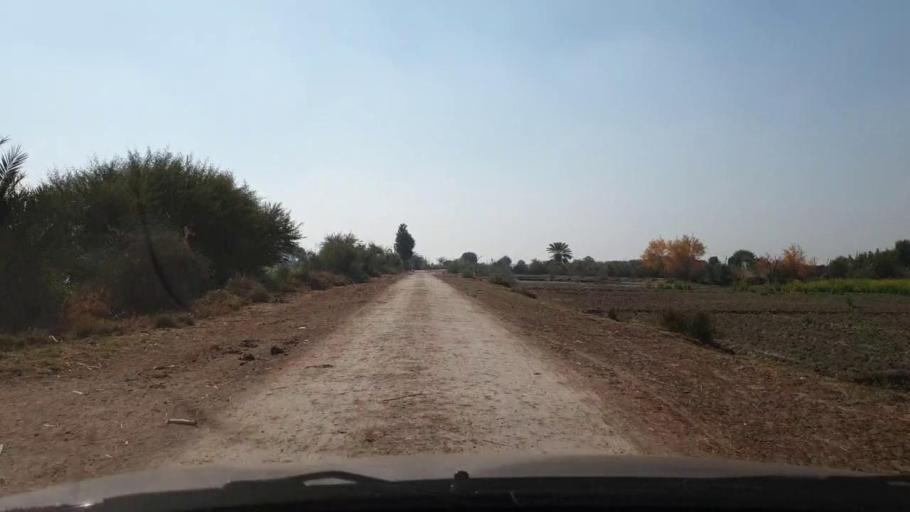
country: PK
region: Sindh
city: Jhol
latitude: 25.9236
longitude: 68.7948
